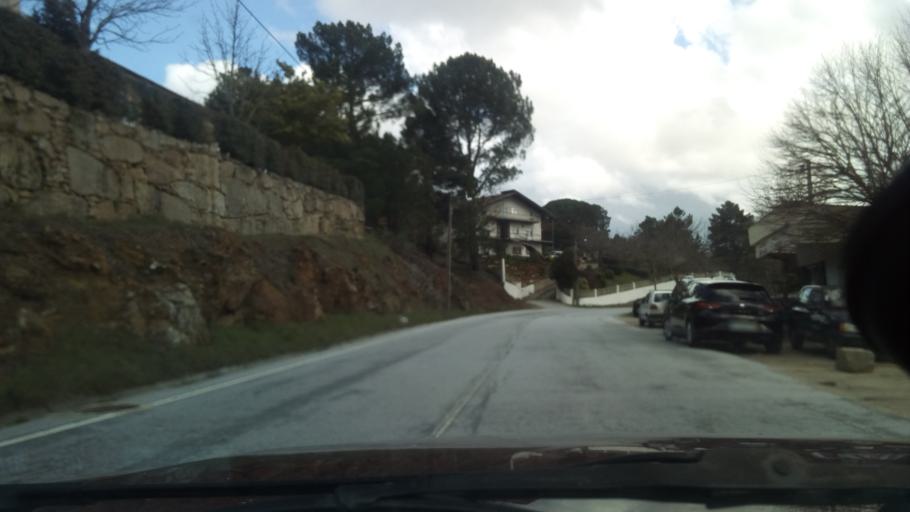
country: PT
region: Guarda
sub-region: Guarda
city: Guarda
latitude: 40.5413
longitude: -7.3158
